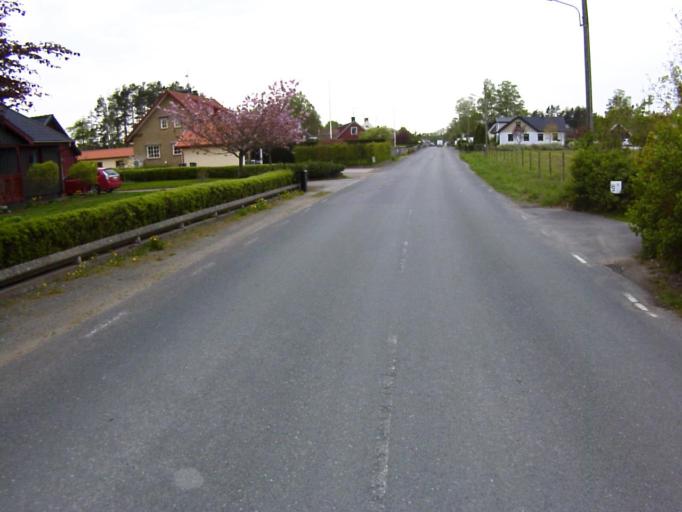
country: SE
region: Skane
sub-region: Kristianstads Kommun
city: Onnestad
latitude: 55.9319
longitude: 14.0021
